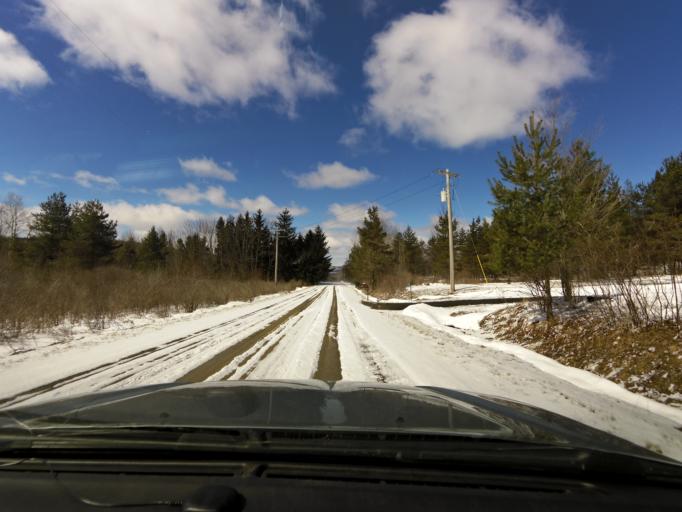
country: US
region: New York
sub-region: Cattaraugus County
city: Franklinville
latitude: 42.3428
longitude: -78.4025
